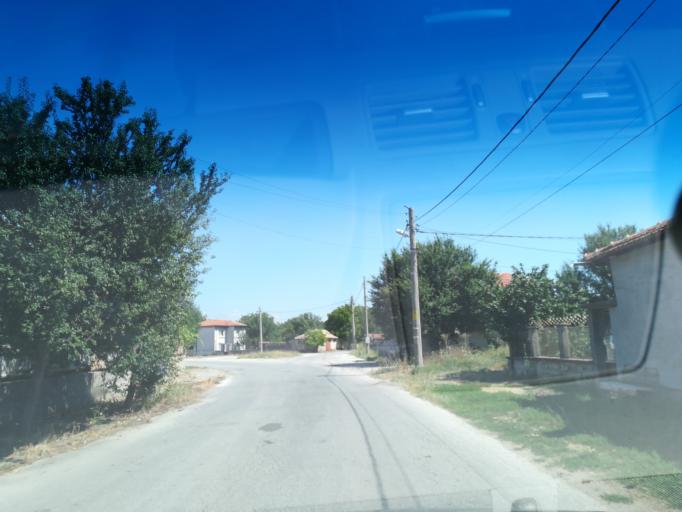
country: BG
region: Plovdiv
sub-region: Obshtina Sadovo
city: Sadovo
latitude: 42.0118
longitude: 25.0446
